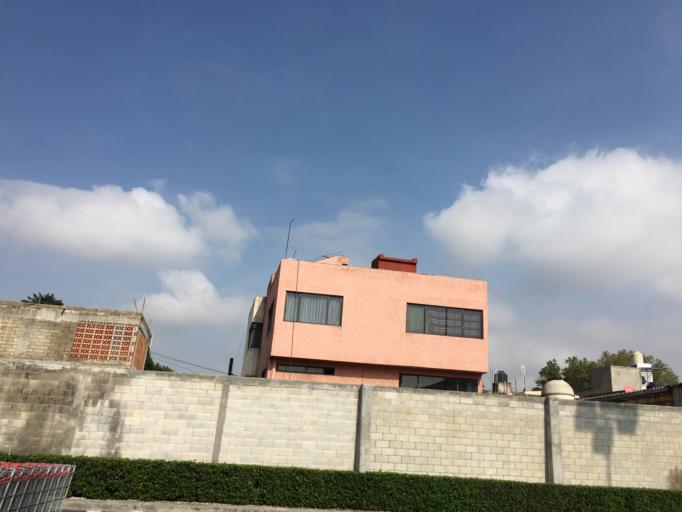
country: MX
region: Mexico City
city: Tlalpan
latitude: 19.2853
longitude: -99.1386
